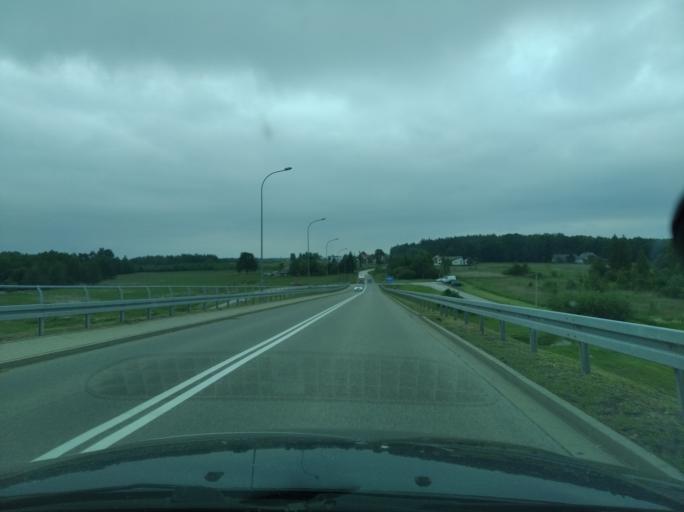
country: PL
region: Subcarpathian Voivodeship
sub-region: Powiat ropczycko-sedziszowski
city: Sedziszow Malopolski
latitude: 50.1088
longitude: 21.6712
